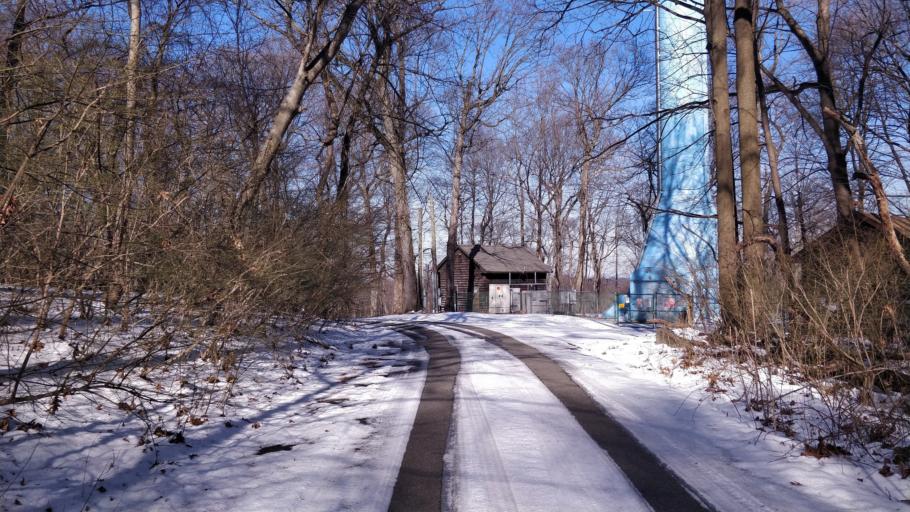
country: US
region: New York
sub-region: Nassau County
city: Old Westbury
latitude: 40.8025
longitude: -73.6057
